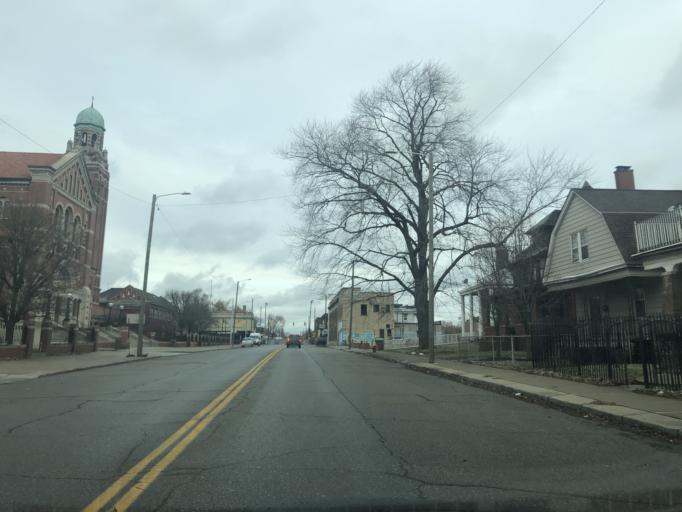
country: US
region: Michigan
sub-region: Wayne County
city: River Rouge
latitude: 42.3167
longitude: -83.1010
